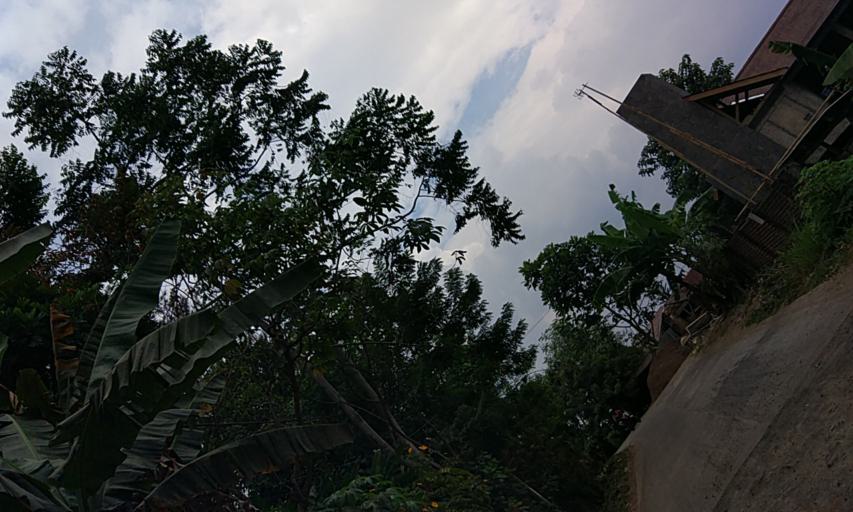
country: ID
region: West Java
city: Bandung
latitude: -6.8789
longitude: 107.6933
